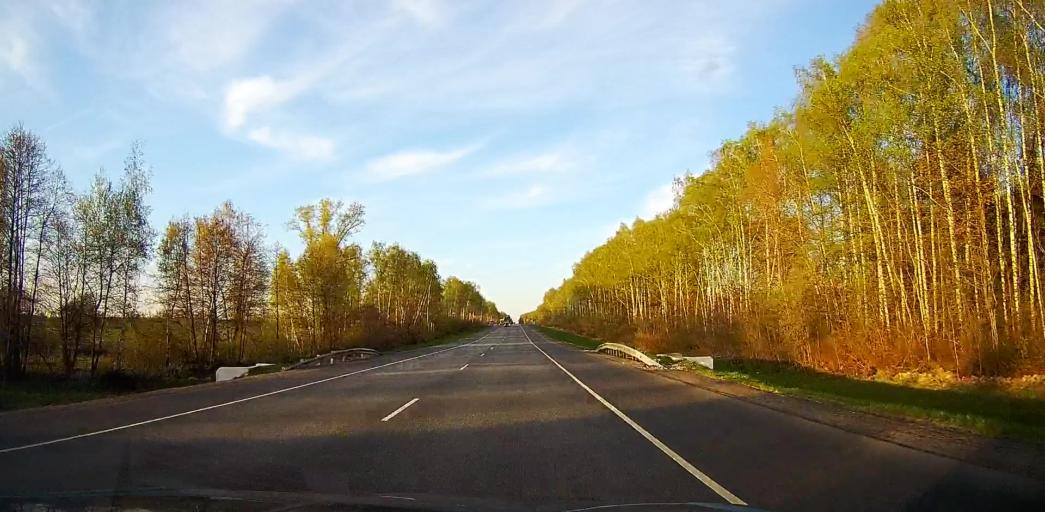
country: RU
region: Moskovskaya
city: Meshcherino
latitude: 55.2404
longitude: 38.4288
